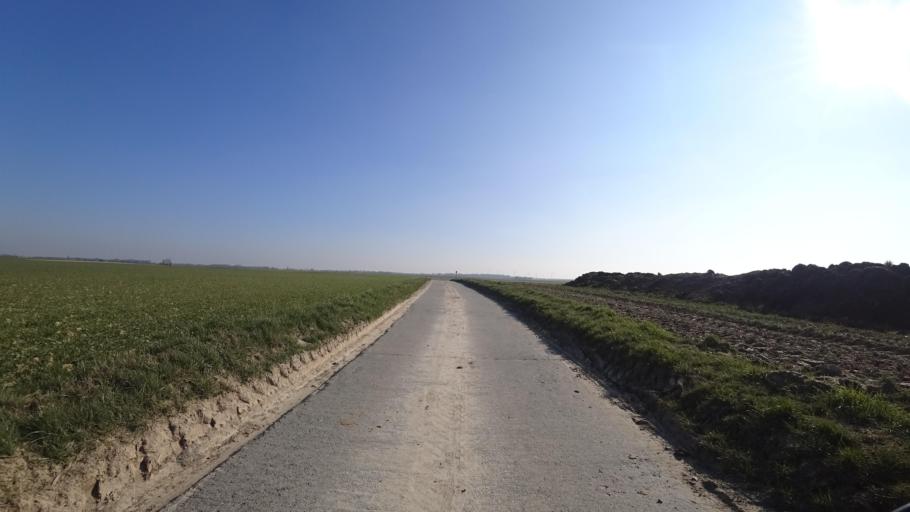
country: BE
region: Wallonia
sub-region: Province du Brabant Wallon
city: Chastre
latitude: 50.5913
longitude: 4.6140
